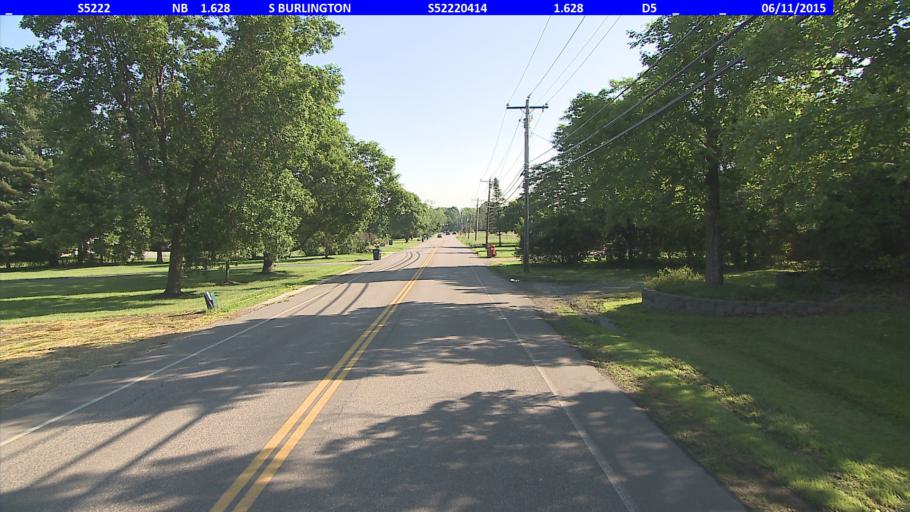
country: US
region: Vermont
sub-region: Chittenden County
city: South Burlington
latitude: 44.4401
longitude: -73.1900
